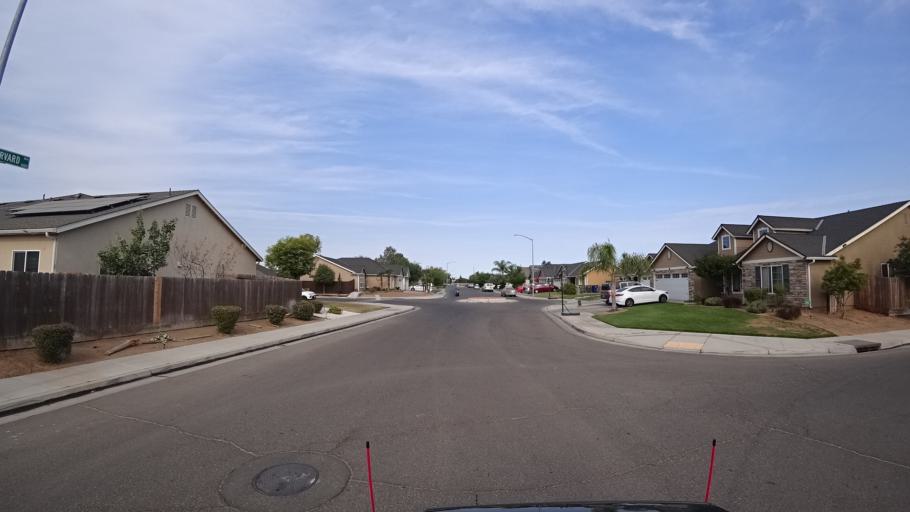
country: US
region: California
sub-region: Fresno County
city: West Park
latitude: 36.7740
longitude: -119.8762
